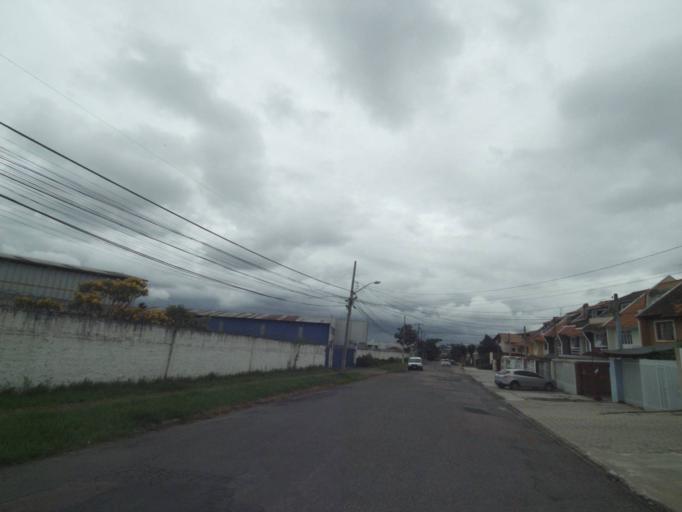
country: BR
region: Parana
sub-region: Curitiba
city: Curitiba
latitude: -25.4916
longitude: -49.3135
